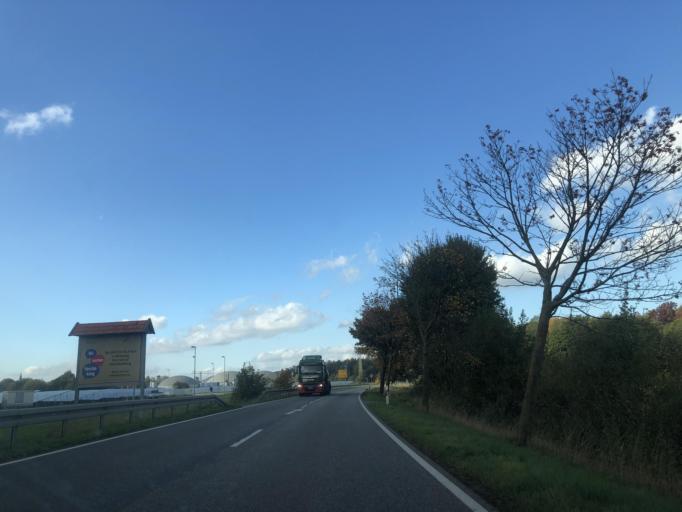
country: DE
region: Mecklenburg-Vorpommern
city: Wittenburg
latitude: 53.5099
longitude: 11.0929
